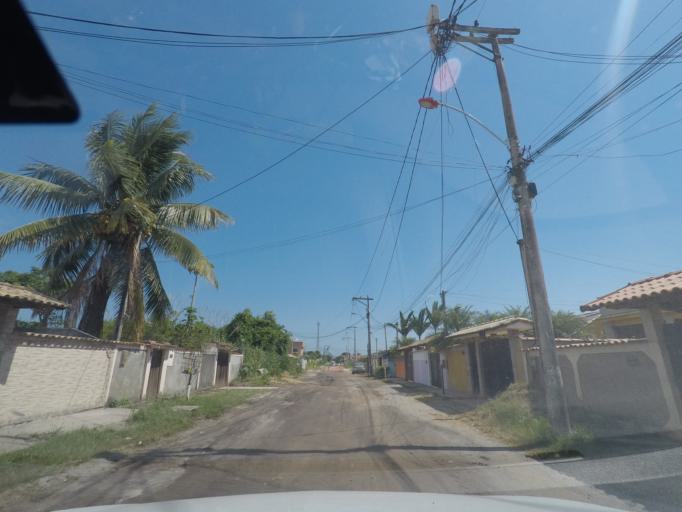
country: BR
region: Rio de Janeiro
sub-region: Marica
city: Marica
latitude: -22.9576
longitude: -42.9631
